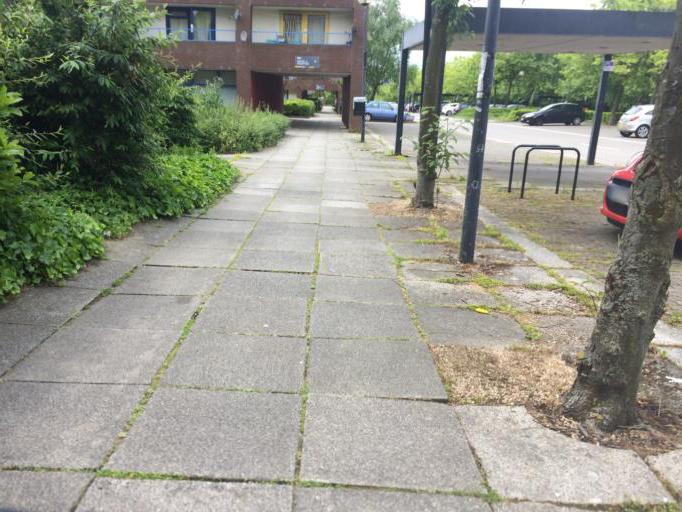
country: GB
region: England
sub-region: Milton Keynes
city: Milton Keynes
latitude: 52.0432
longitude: -0.7636
